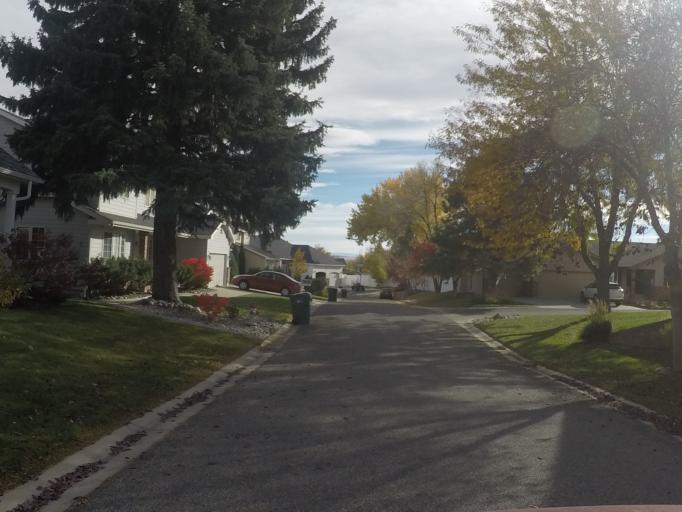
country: US
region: Montana
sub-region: Yellowstone County
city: Billings
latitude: 45.7967
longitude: -108.5599
